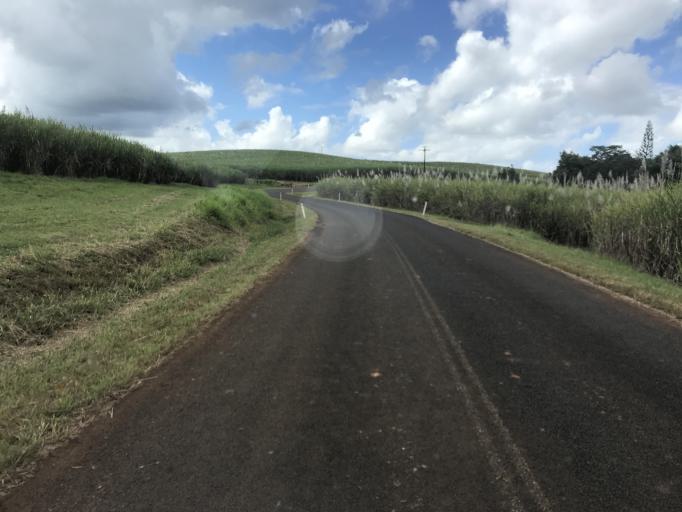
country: AU
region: Queensland
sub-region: Cassowary Coast
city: Innisfail
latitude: -17.5492
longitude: 145.8733
